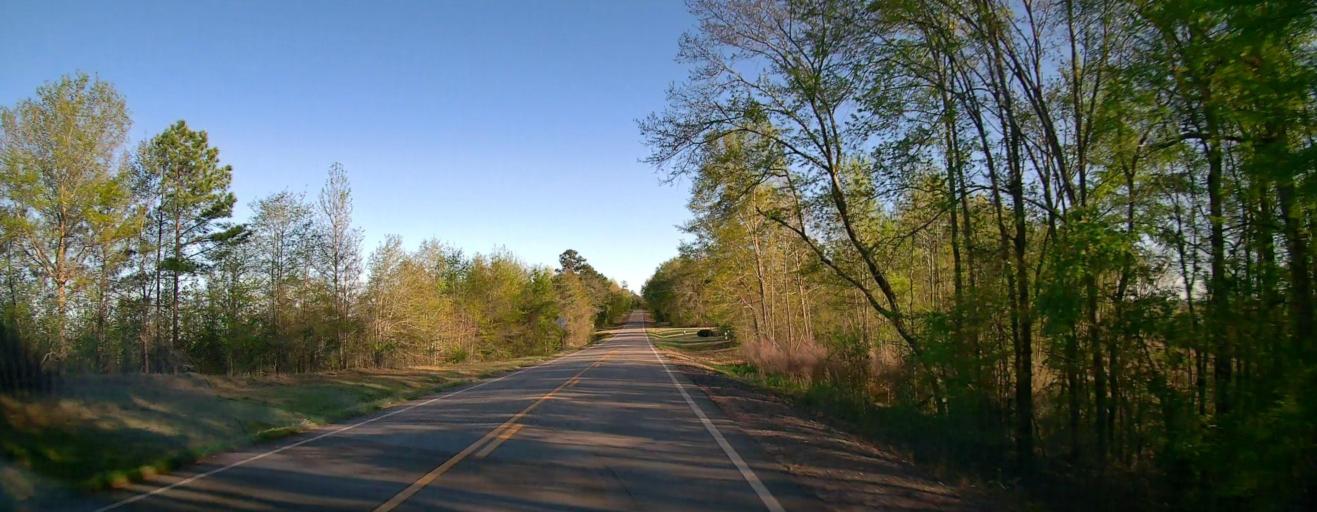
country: US
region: Georgia
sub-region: Wilkinson County
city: Irwinton
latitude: 32.8554
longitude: -83.0665
